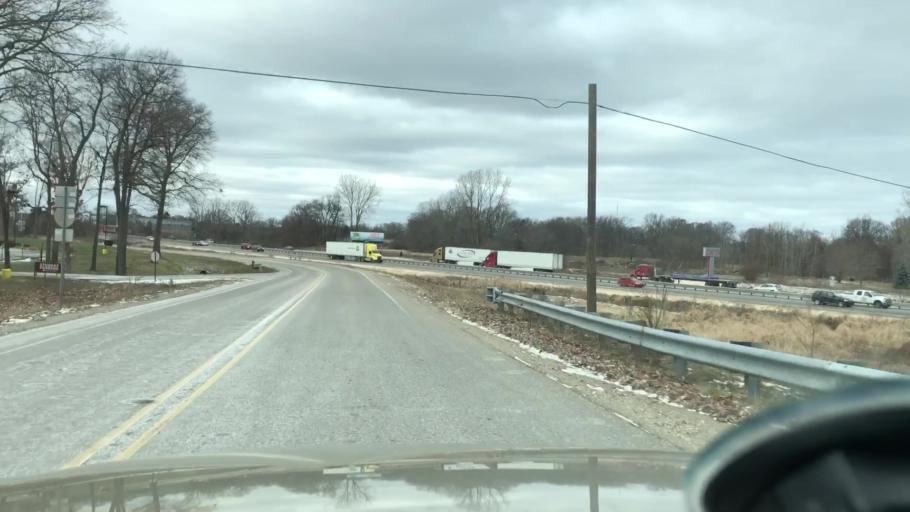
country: US
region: Michigan
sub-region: Jackson County
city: Jackson
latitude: 42.2758
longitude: -84.3651
